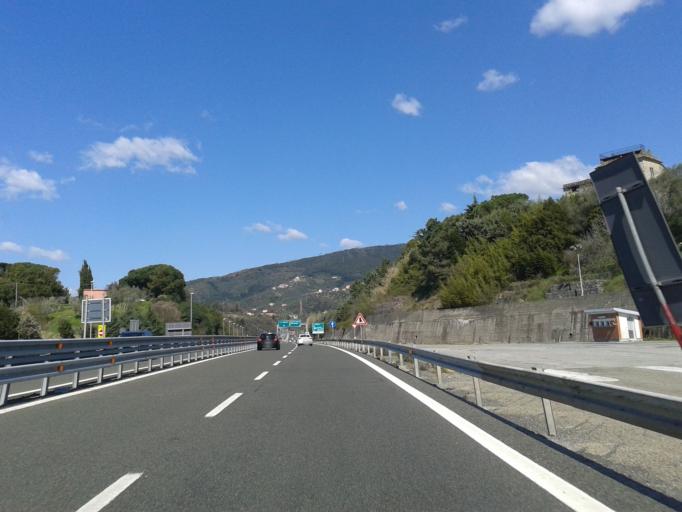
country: IT
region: Liguria
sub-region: Provincia di Genova
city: Casarza Ligure
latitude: 44.2716
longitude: 9.4248
